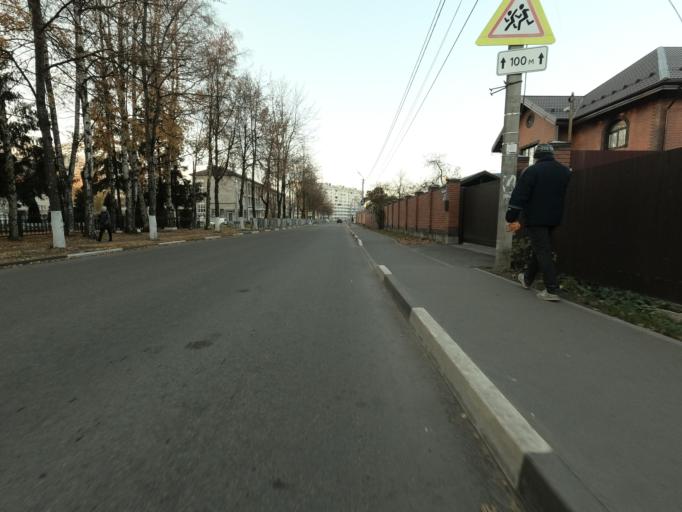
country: RU
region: Leningrad
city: Kirovsk
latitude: 59.8779
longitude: 30.9909
